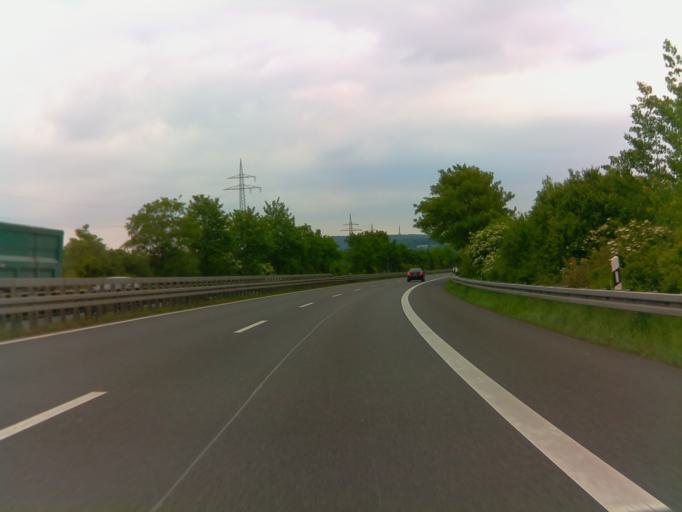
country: DE
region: Hesse
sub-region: Regierungsbezirk Giessen
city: Marburg an der Lahn
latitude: 50.7662
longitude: 8.7480
